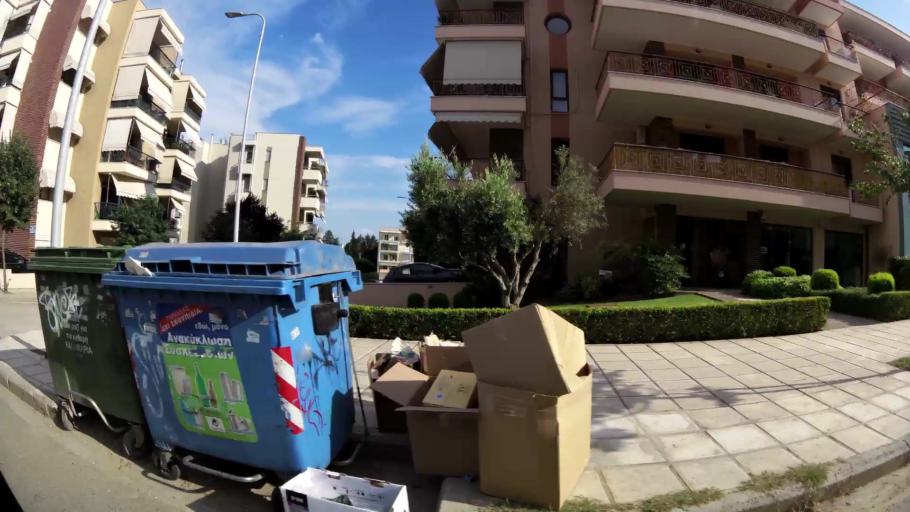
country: GR
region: Central Macedonia
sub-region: Nomos Thessalonikis
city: Kalamaria
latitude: 40.5696
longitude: 22.9696
